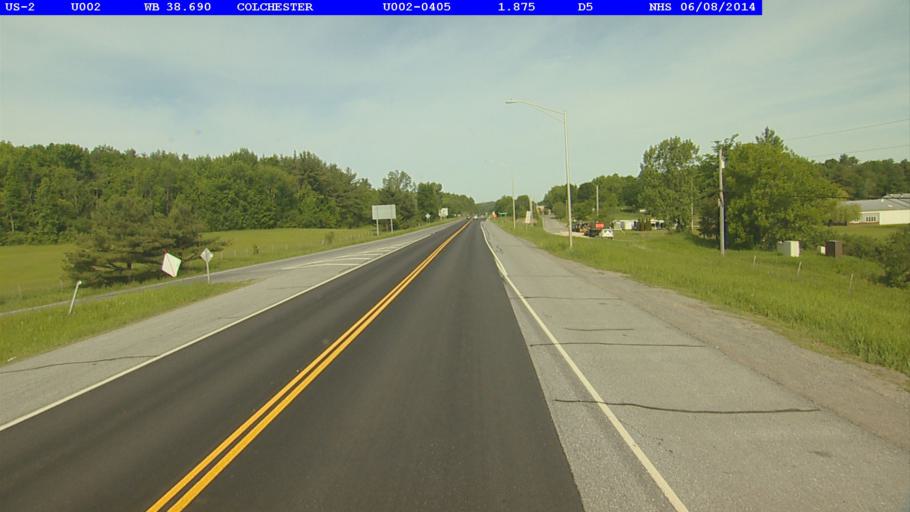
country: US
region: Vermont
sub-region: Chittenden County
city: Colchester
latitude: 44.5905
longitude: -73.1724
